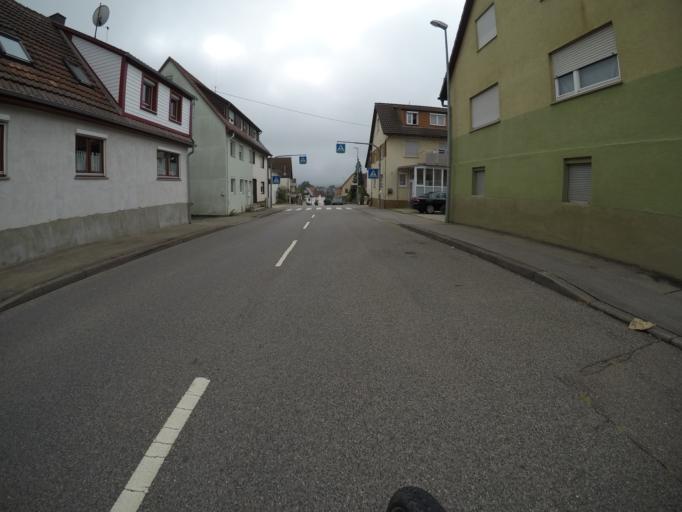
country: DE
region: Baden-Wuerttemberg
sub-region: Regierungsbezirk Stuttgart
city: Gartringen
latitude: 48.6418
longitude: 8.8935
